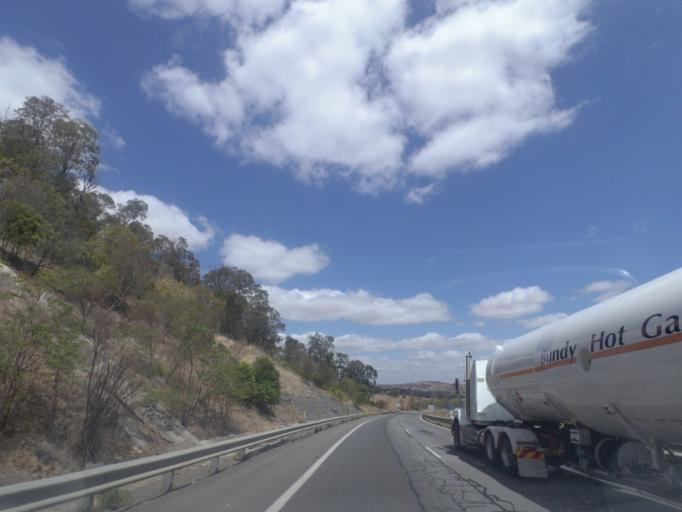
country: AU
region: Queensland
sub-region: Ipswich
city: Thagoona
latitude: -27.5642
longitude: 152.5567
